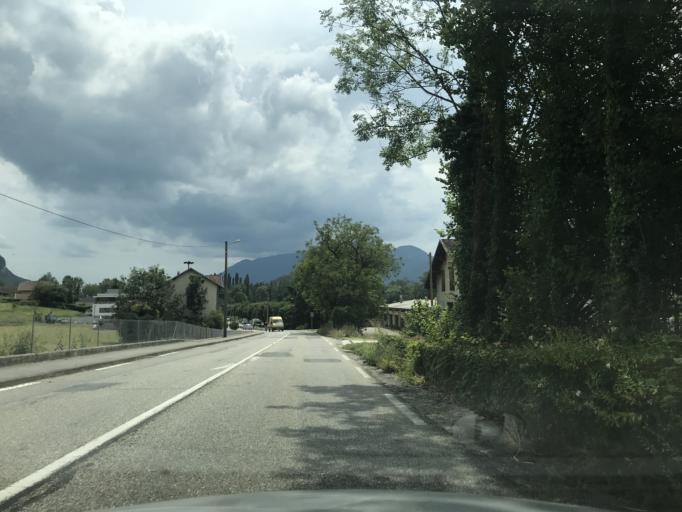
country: FR
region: Rhone-Alpes
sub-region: Departement de la Savoie
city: Chindrieux
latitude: 45.8155
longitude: 5.8495
